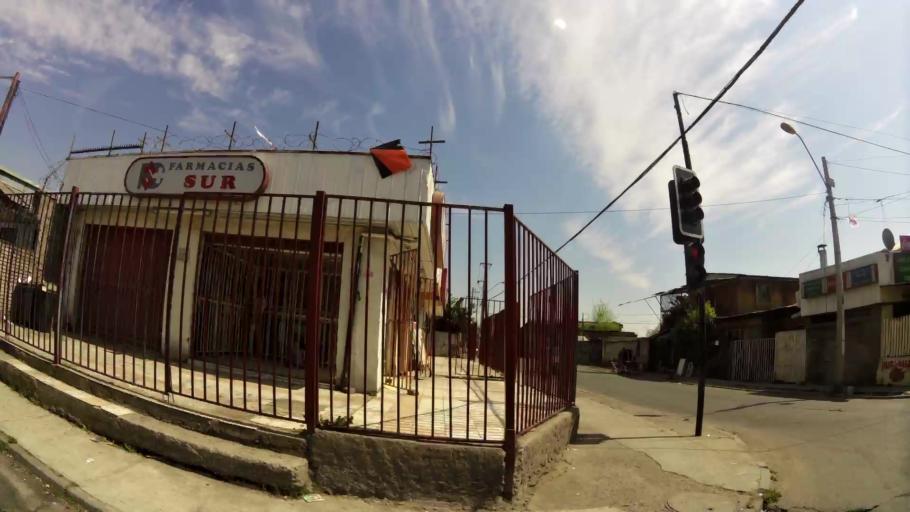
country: CL
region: Santiago Metropolitan
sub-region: Provincia de Santiago
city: La Pintana
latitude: -33.5502
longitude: -70.6533
